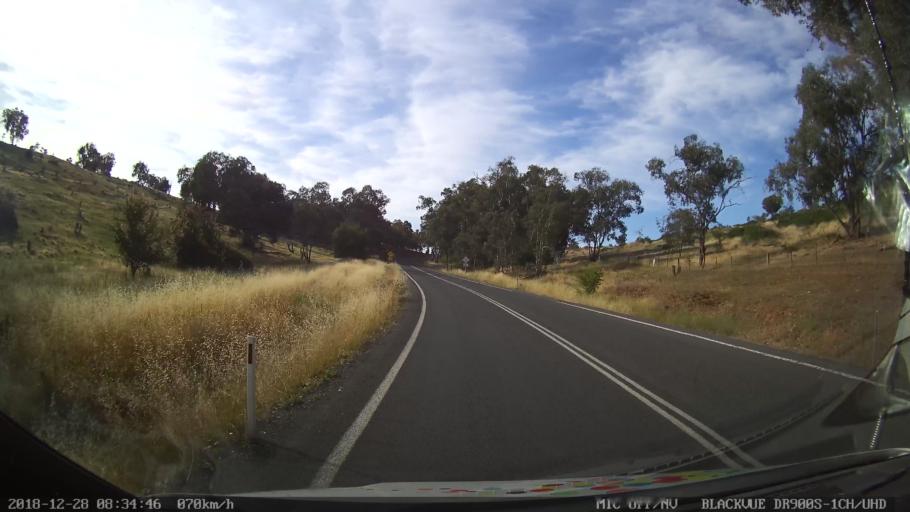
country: AU
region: New South Wales
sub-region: Blayney
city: Blayney
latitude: -33.9780
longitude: 149.3099
